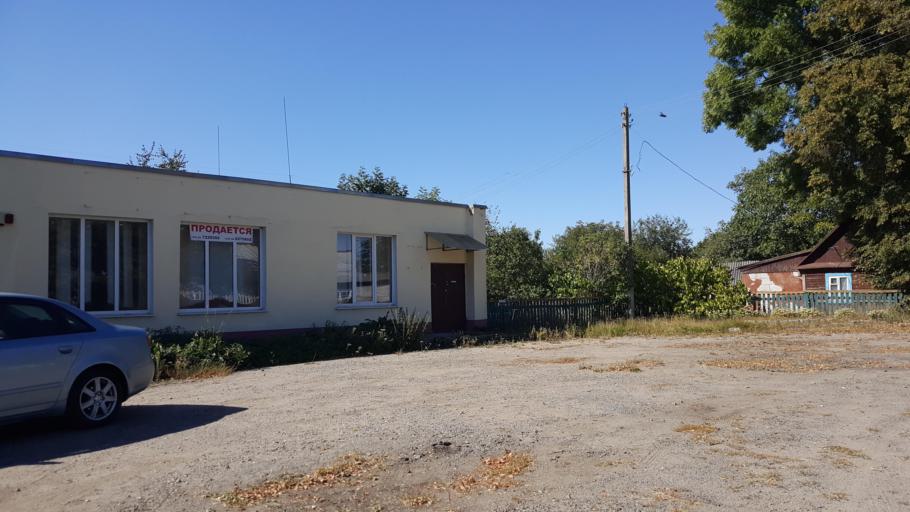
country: BY
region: Brest
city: Vysokaye
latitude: 52.2604
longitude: 23.5342
